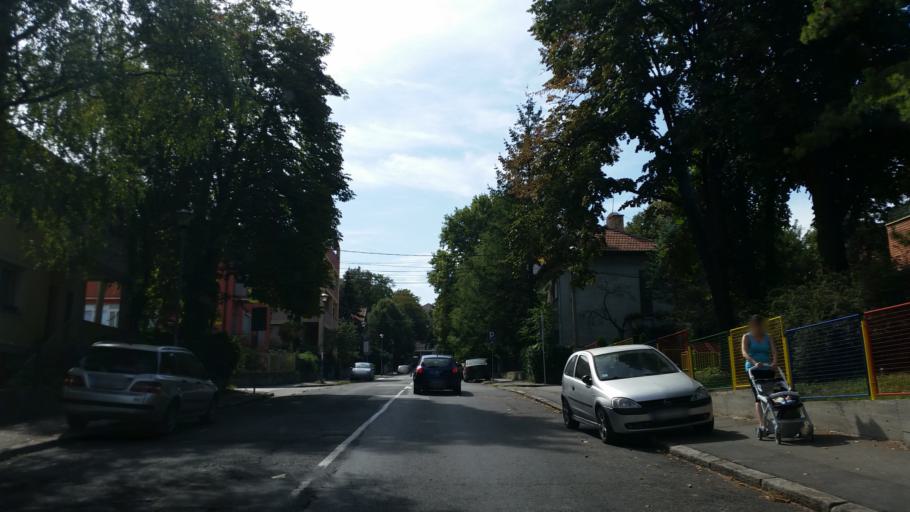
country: RS
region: Central Serbia
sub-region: Belgrade
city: Palilula
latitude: 44.8118
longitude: 20.5168
